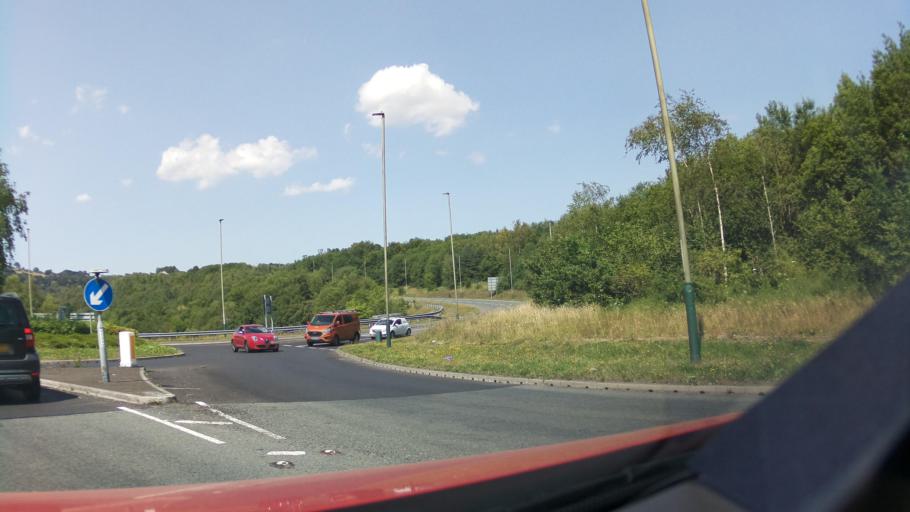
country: GB
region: Wales
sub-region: Caerphilly County Borough
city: Bargoed
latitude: 51.6880
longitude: -3.2258
